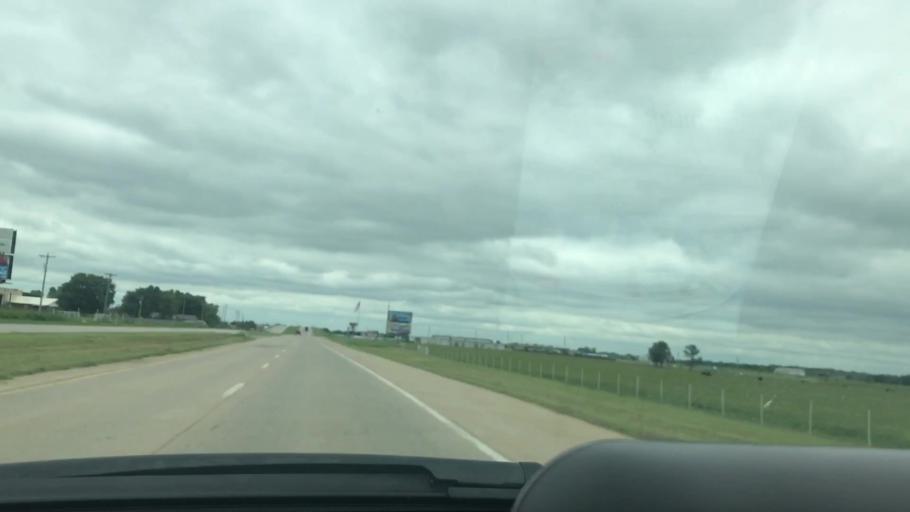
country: US
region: Oklahoma
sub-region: Craig County
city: Vinita
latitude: 36.5490
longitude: -95.2201
